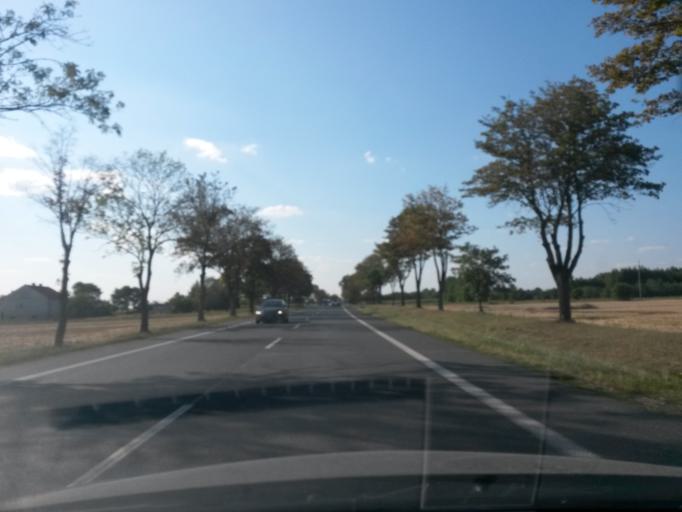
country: PL
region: Masovian Voivodeship
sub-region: Powiat sierpecki
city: Zawidz
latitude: 52.7939
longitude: 19.8716
